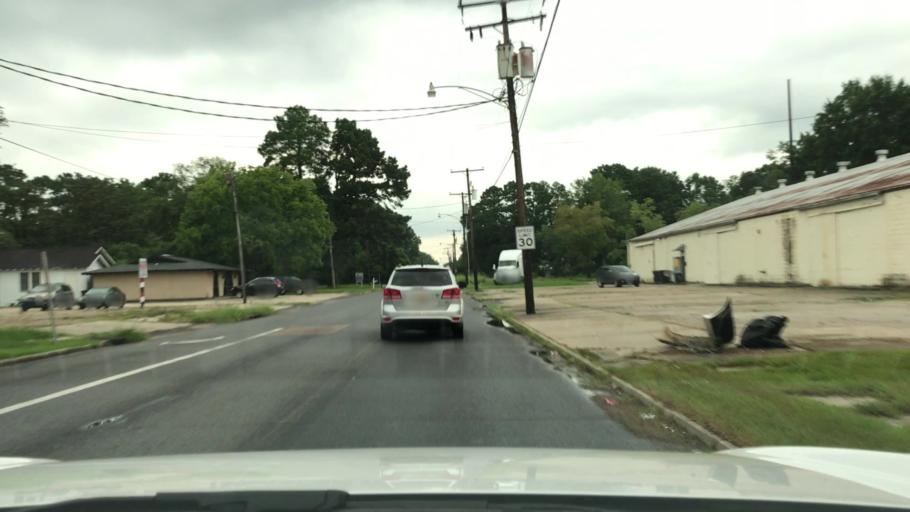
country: US
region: Louisiana
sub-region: East Baton Rouge Parish
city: Merrydale
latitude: 30.4750
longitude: -91.1174
